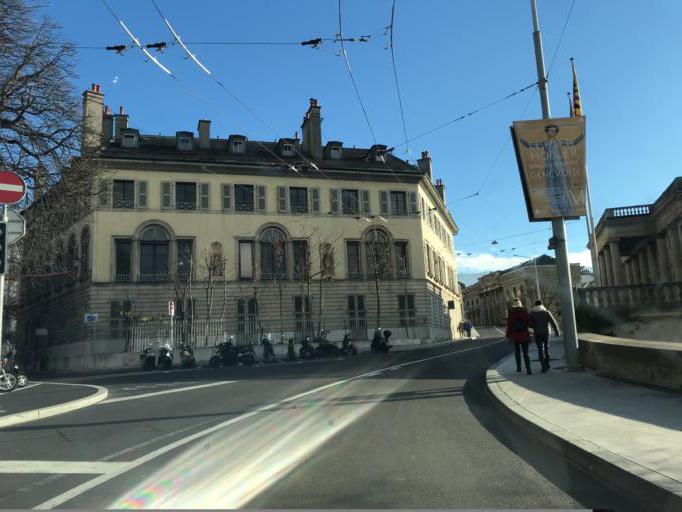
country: CH
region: Geneva
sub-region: Geneva
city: Geneve
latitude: 46.1999
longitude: 6.1470
